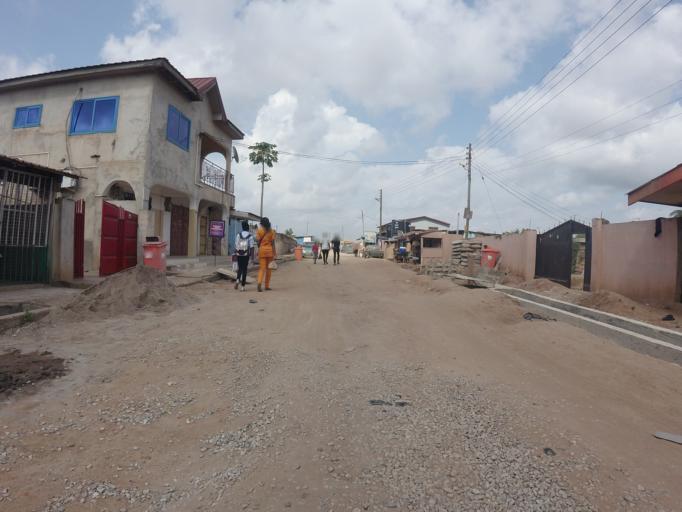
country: GH
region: Greater Accra
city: Dome
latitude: 5.6146
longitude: -0.2444
